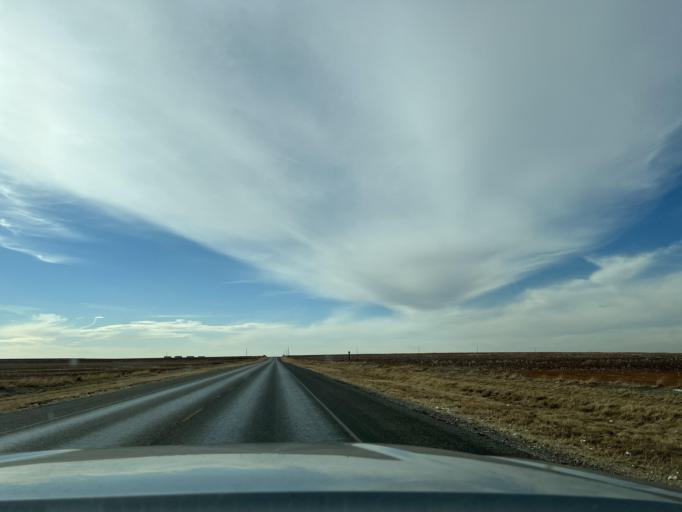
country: US
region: Texas
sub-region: Fisher County
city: Roby
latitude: 32.7418
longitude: -100.4498
